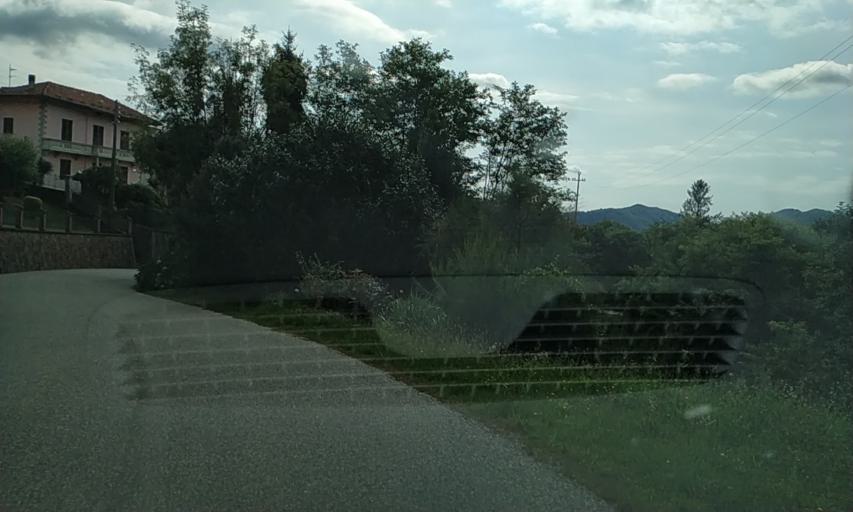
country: IT
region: Piedmont
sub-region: Provincia di Biella
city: Frazione Chiesa
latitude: 45.6921
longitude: 8.2137
